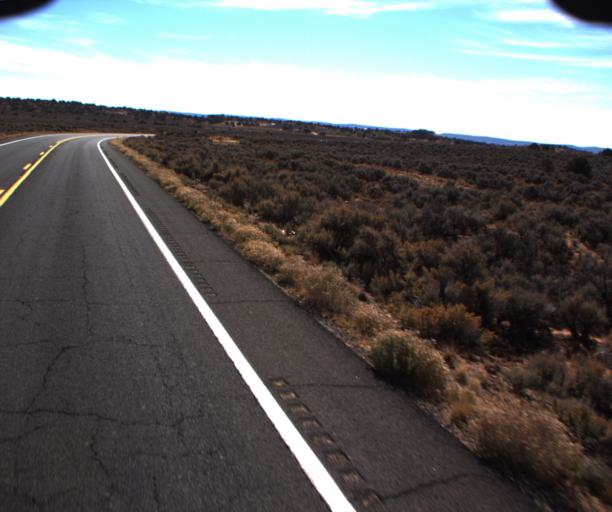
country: US
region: Arizona
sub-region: Coconino County
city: Kaibito
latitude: 36.5525
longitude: -110.7047
